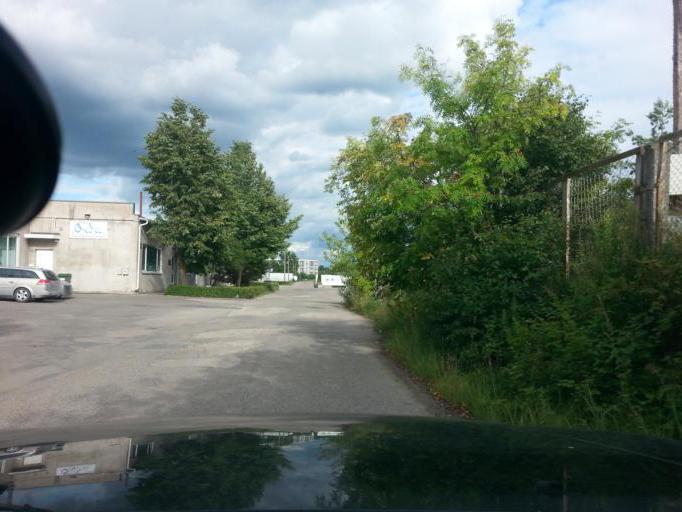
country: LV
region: Stopini
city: Ulbroka
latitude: 56.9556
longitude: 24.2300
